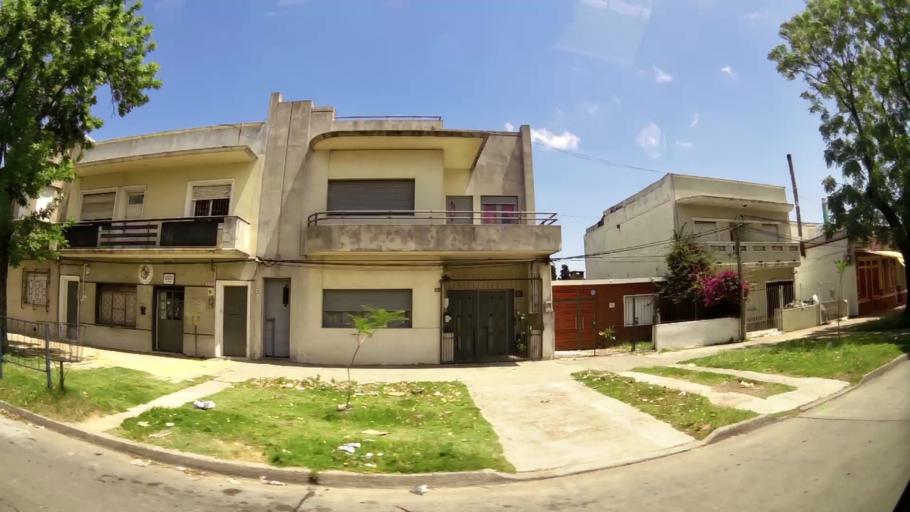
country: UY
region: Montevideo
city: Montevideo
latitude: -34.8577
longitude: -56.2267
